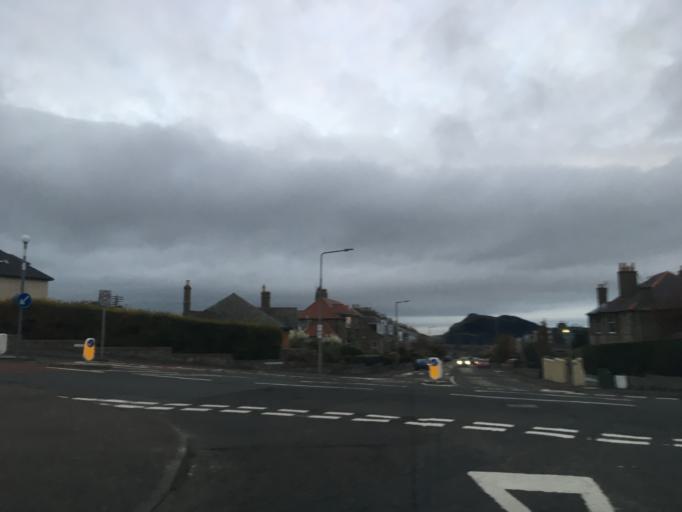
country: GB
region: Scotland
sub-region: Midlothian
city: Loanhead
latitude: 55.9116
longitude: -3.1686
